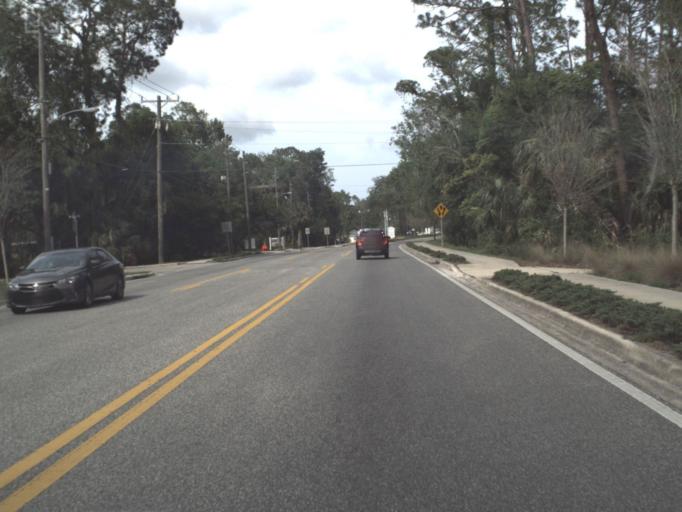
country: US
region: Florida
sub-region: Flagler County
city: Bunnell
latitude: 29.4714
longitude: -81.2524
